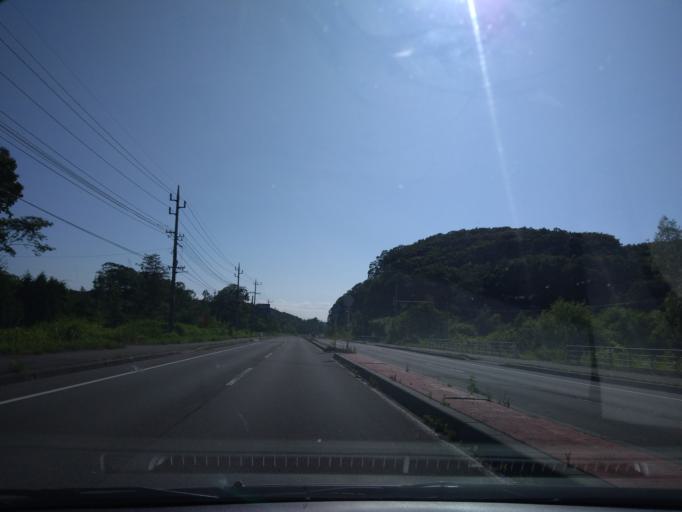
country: JP
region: Hokkaido
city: Kitahiroshima
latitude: 42.9794
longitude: 141.5188
